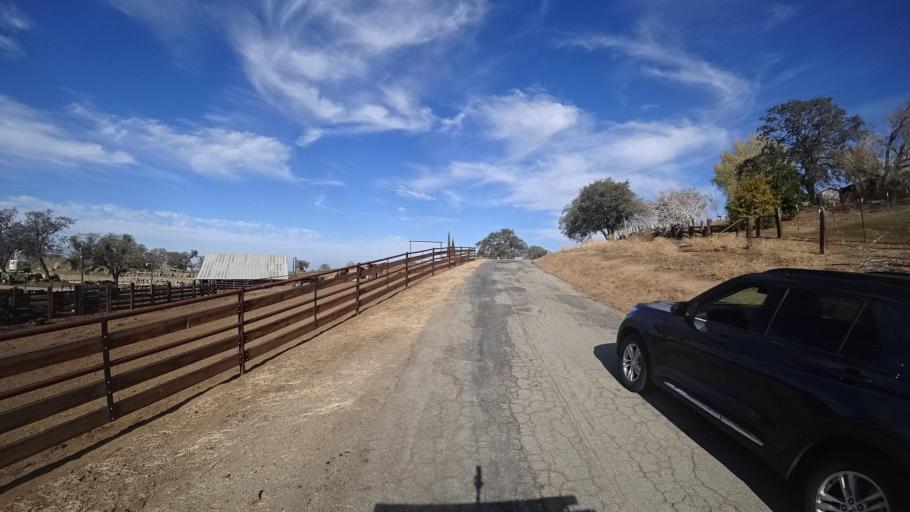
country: US
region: California
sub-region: Kern County
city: Oildale
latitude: 35.6184
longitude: -118.8487
